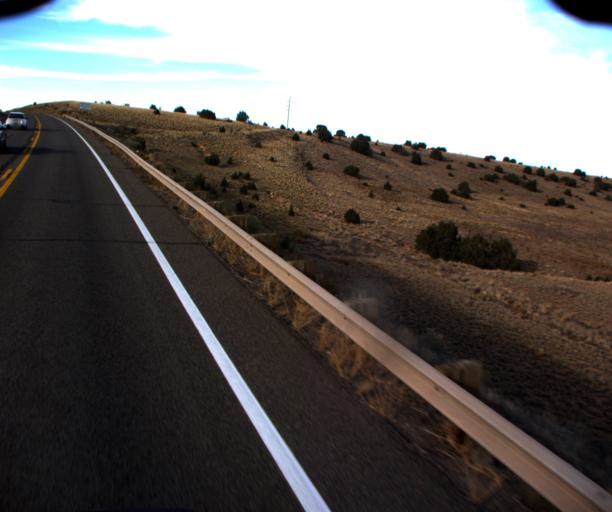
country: US
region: New Mexico
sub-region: San Juan County
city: Shiprock
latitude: 36.8763
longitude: -109.0467
